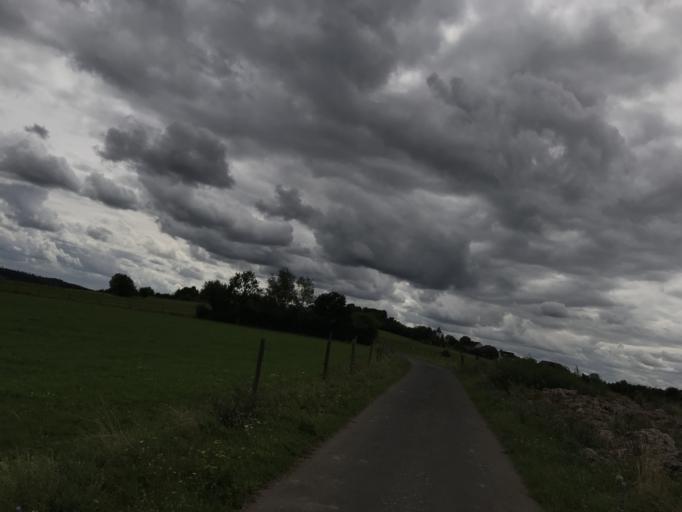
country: DE
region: Hesse
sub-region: Regierungsbezirk Giessen
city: Grunberg
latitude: 50.6230
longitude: 8.9719
